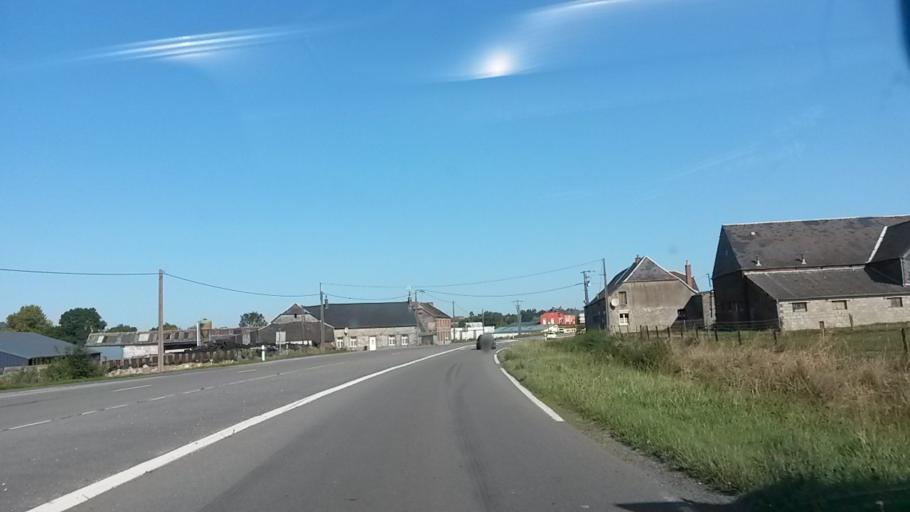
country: FR
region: Nord-Pas-de-Calais
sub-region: Departement du Nord
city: Avesnes-sur-Helpe
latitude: 50.0667
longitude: 3.9291
